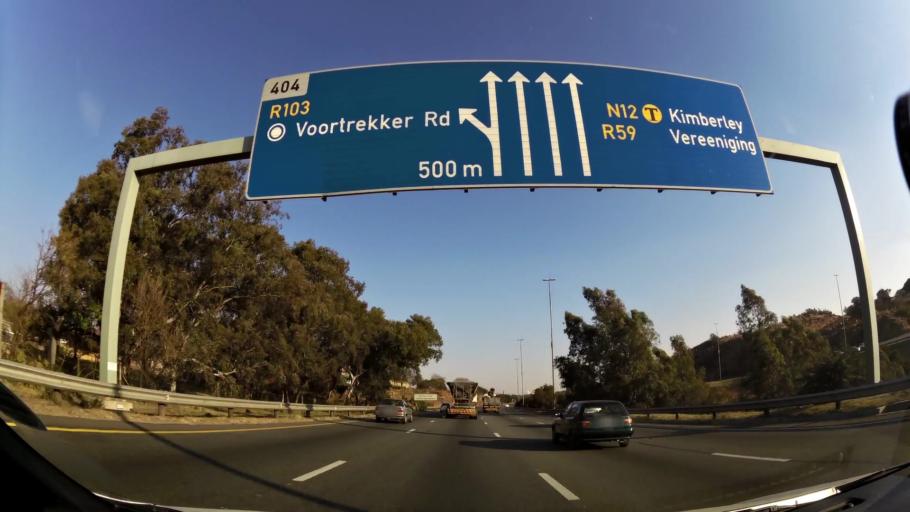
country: ZA
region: Gauteng
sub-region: Ekurhuleni Metropolitan Municipality
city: Germiston
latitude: -26.2522
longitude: 28.1225
